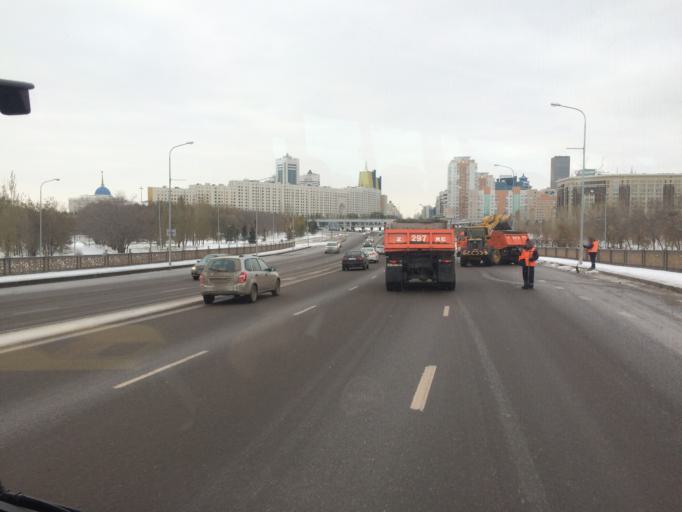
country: KZ
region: Astana Qalasy
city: Astana
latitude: 51.1362
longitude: 71.4419
